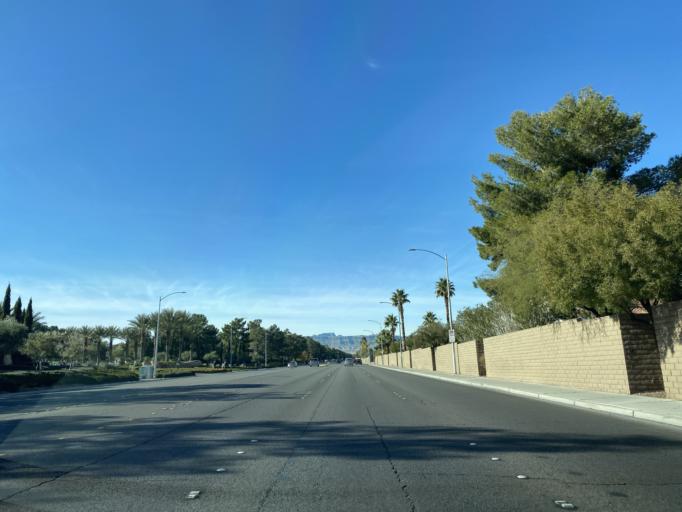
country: US
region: Nevada
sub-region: Clark County
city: Spring Valley
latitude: 36.0997
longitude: -115.2560
